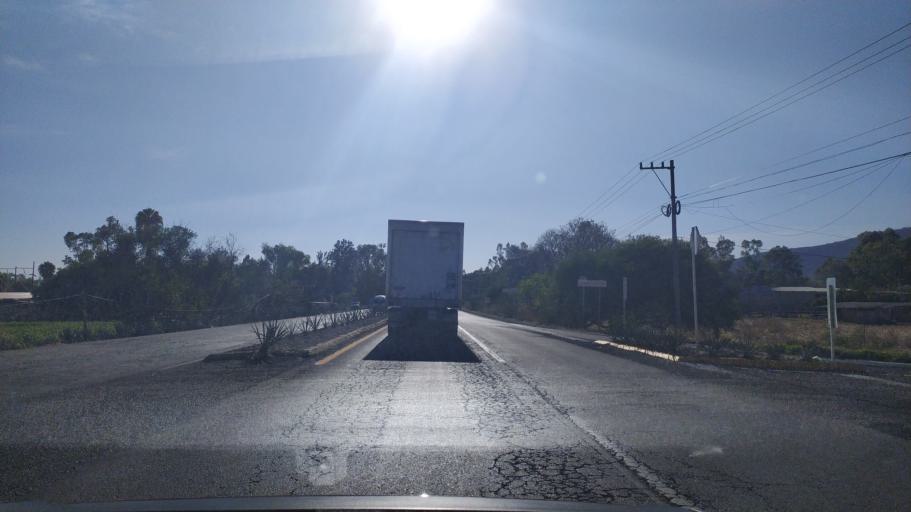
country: MX
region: Jalisco
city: Jamay
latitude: 20.2941
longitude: -102.6728
